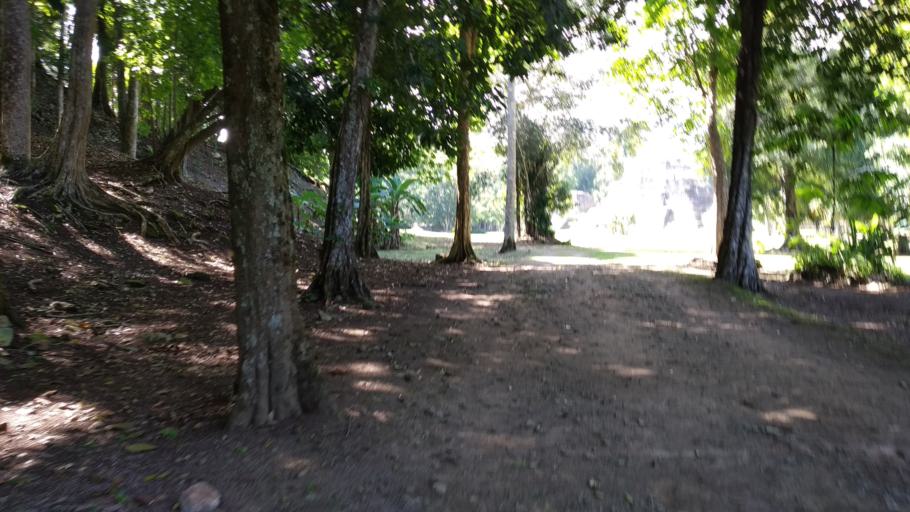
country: GT
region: Peten
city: Melchor de Mencos
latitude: 16.7627
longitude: -89.1191
